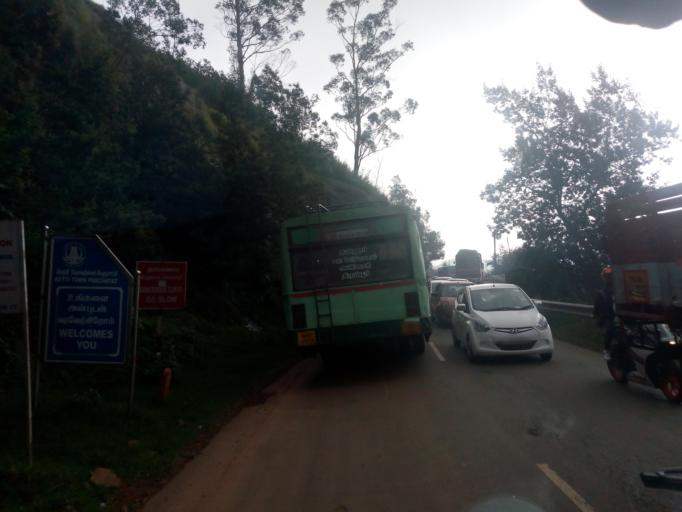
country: IN
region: Tamil Nadu
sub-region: Nilgiri
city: Ooty
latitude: 11.3890
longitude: 76.7214
